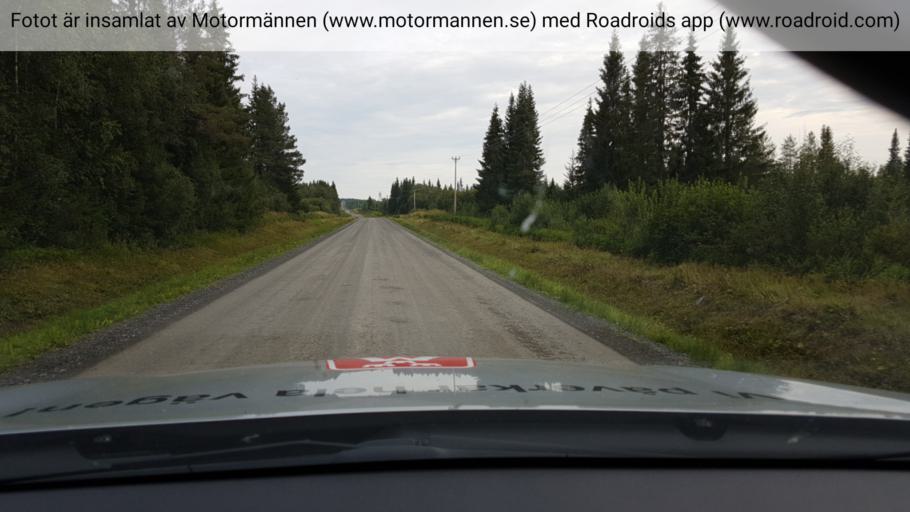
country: SE
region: Jaemtland
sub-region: OEstersunds Kommun
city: Lit
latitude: 63.6356
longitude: 14.9631
